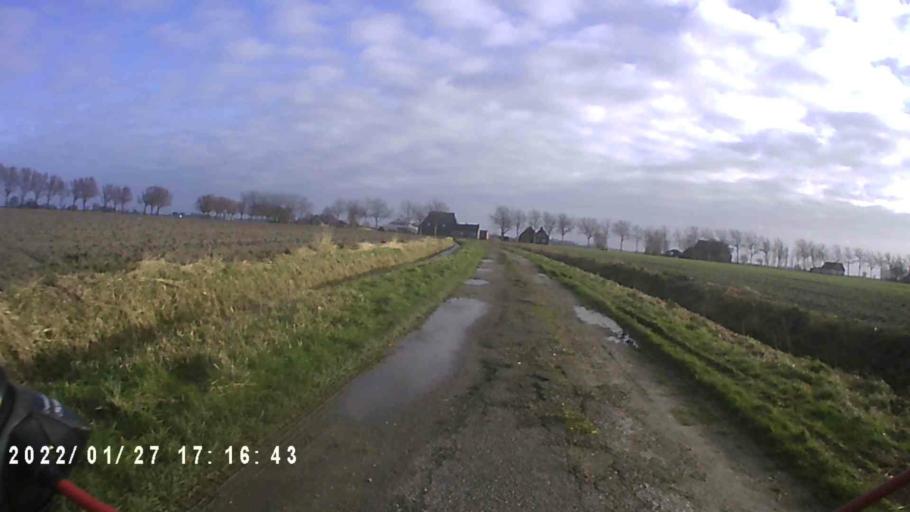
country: NL
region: Friesland
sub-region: Gemeente Dongeradeel
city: Anjum
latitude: 53.3905
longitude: 6.0988
